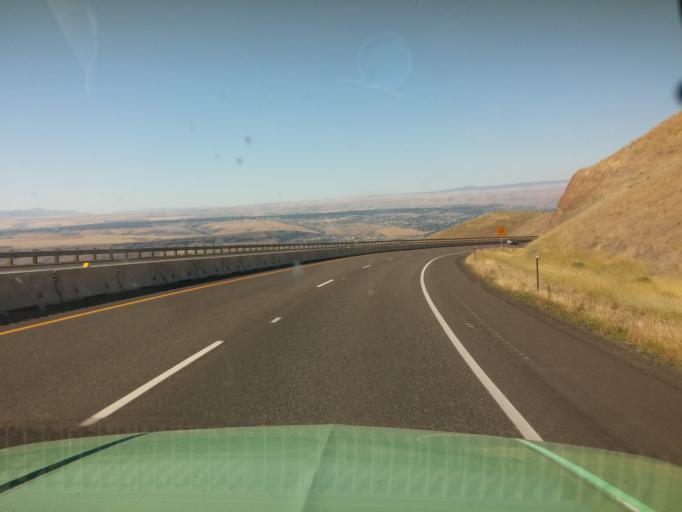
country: US
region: Idaho
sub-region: Nez Perce County
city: Lewiston
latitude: 46.4570
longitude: -116.9583
